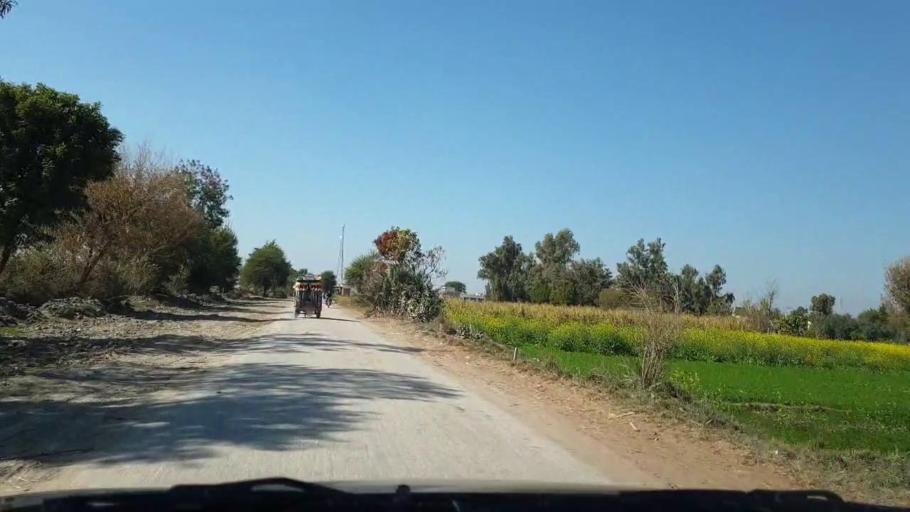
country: PK
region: Sindh
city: Khadro
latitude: 26.1289
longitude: 68.8085
